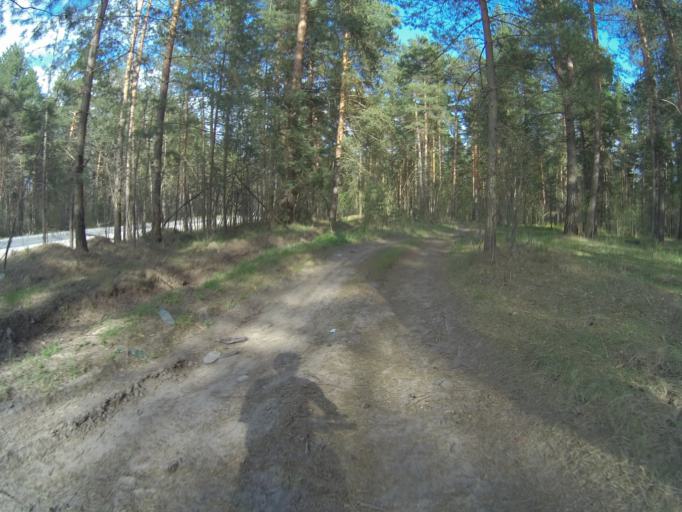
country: RU
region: Vladimir
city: Raduzhnyy
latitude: 56.0288
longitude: 40.4001
